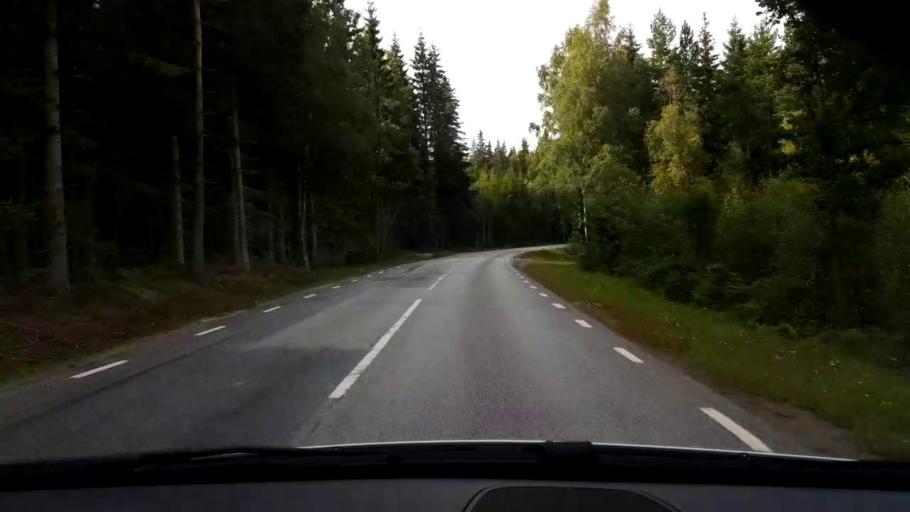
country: SE
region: Joenkoeping
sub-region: Vetlanda Kommun
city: Vetlanda
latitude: 57.3685
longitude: 15.0553
